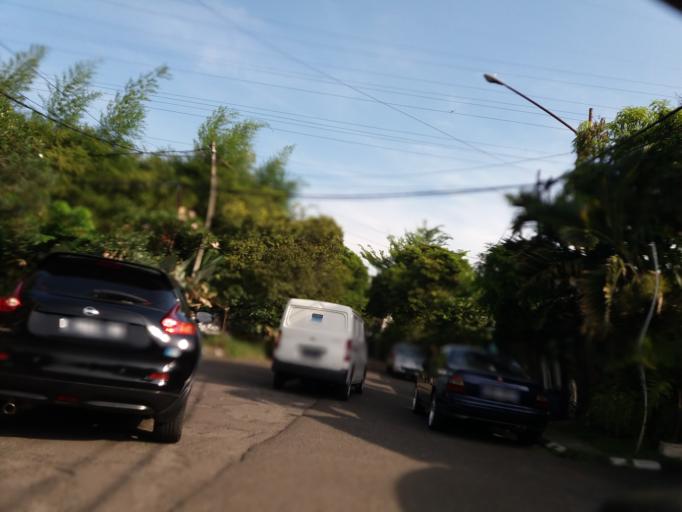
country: ID
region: West Java
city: Bandung
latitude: -6.9634
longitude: 107.6300
